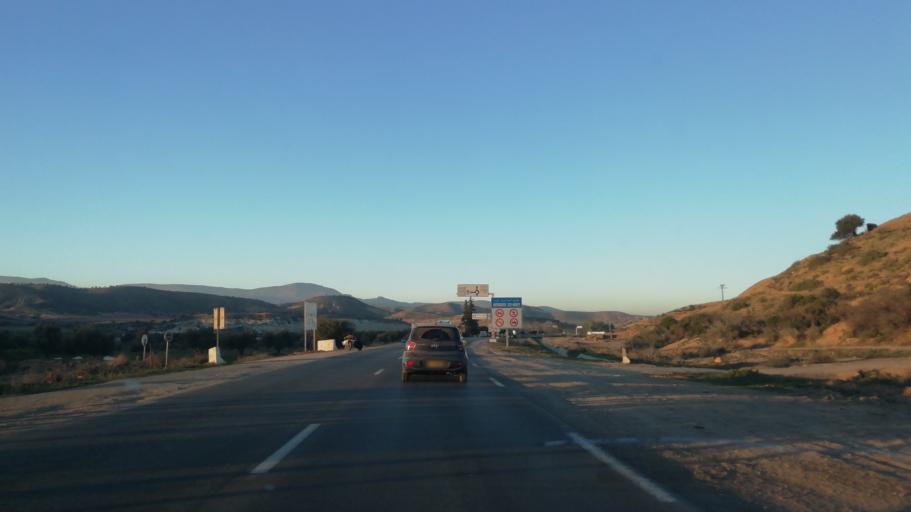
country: DZ
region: Tlemcen
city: Nedroma
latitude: 34.9047
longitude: -1.6406
